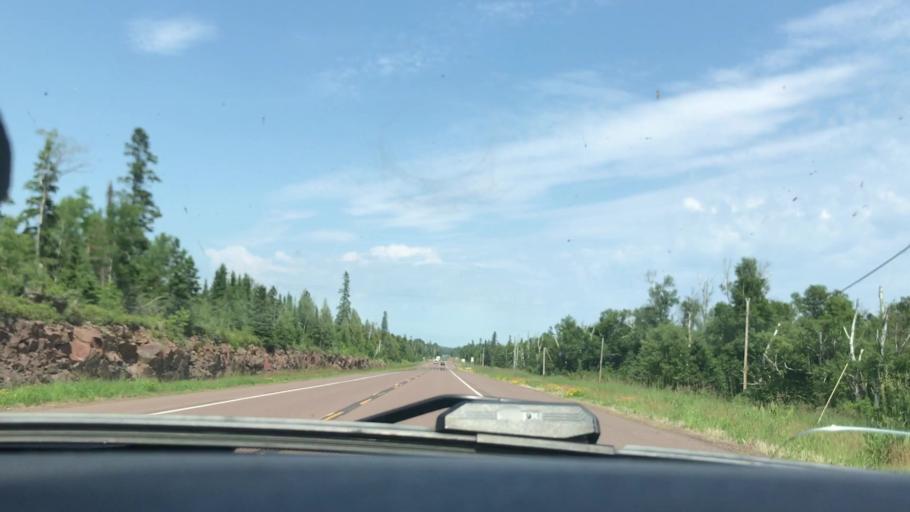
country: US
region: Minnesota
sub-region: Cook County
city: Grand Marais
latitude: 47.6258
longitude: -90.7372
